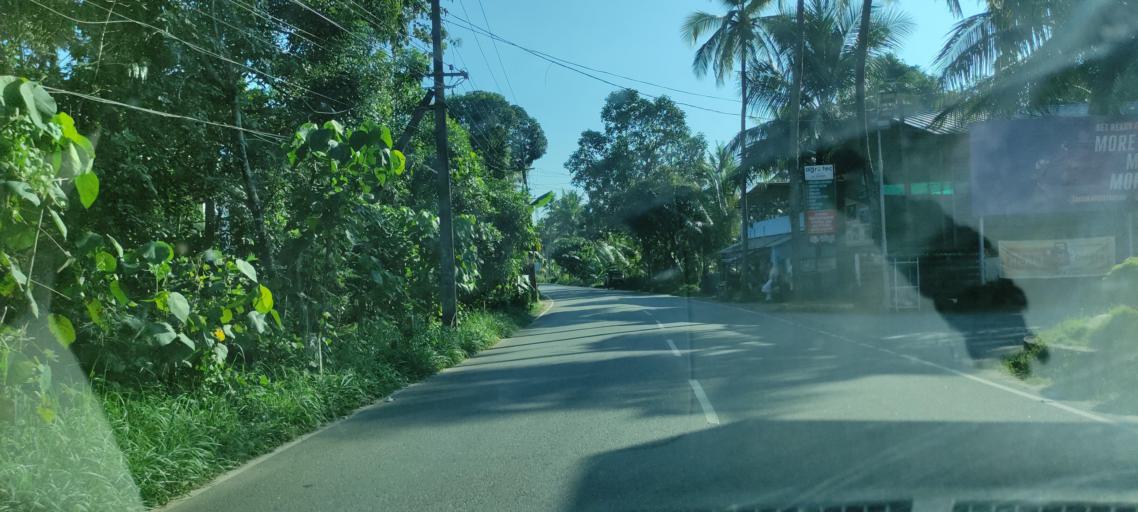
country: IN
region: Kerala
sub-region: Pattanamtitta
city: Adur
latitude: 9.2019
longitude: 76.7447
